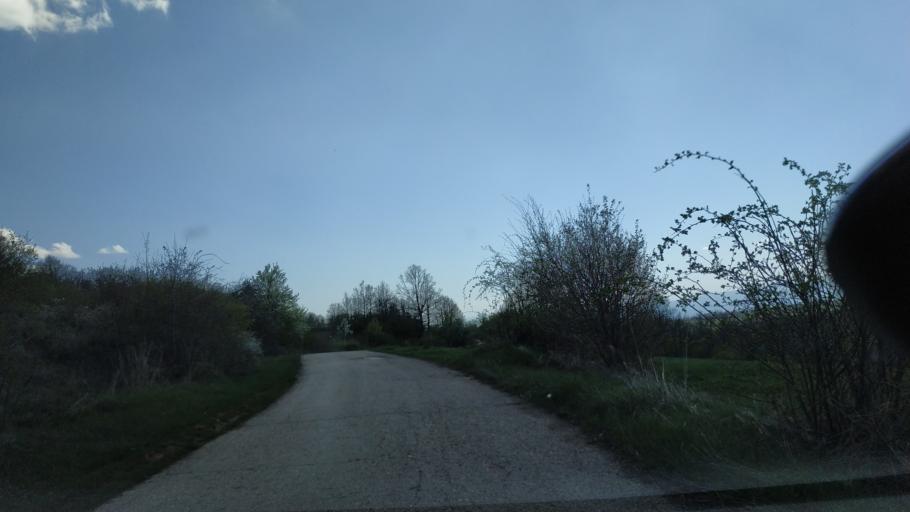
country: RS
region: Central Serbia
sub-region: Zajecarski Okrug
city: Soko Banja
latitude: 43.5642
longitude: 21.8956
